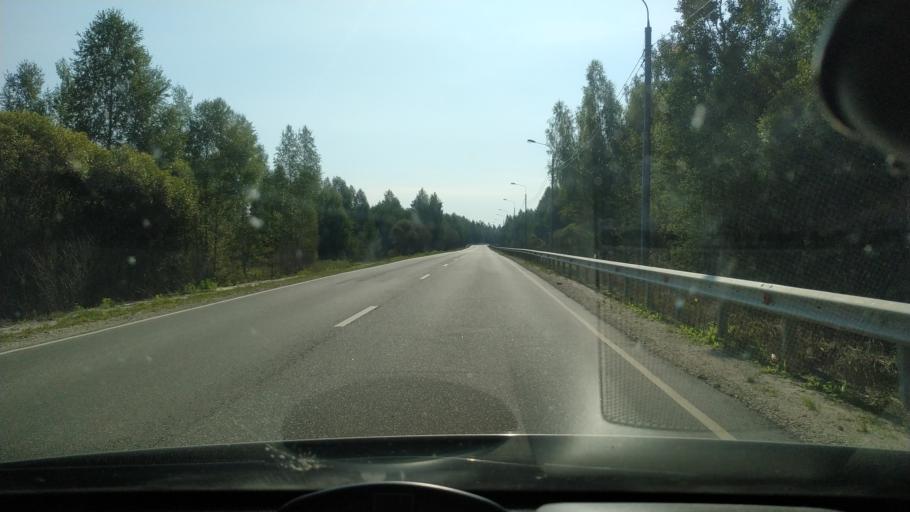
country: RU
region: Moskovskaya
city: Dmitrovskiy Pogost
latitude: 55.2308
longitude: 39.9172
